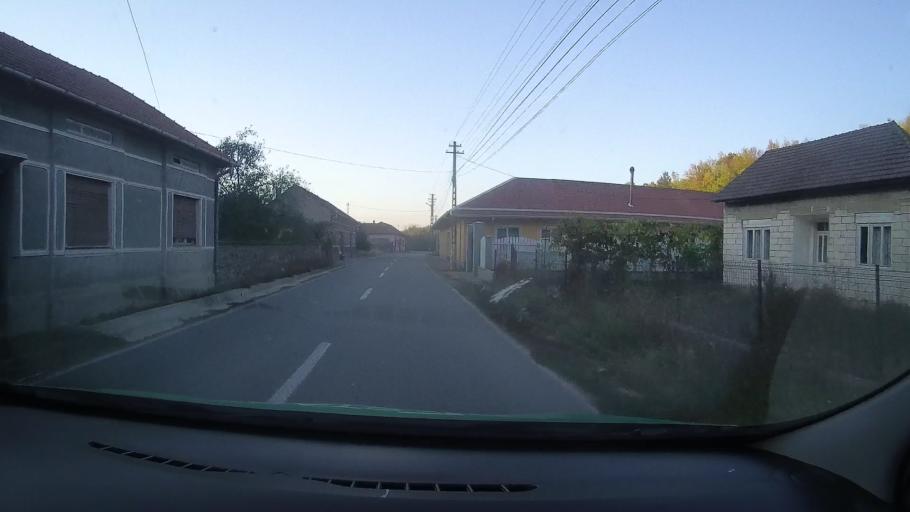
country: RO
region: Timis
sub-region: Comuna Traian Vuia
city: Traian Vuia
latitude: 45.7612
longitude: 22.0980
